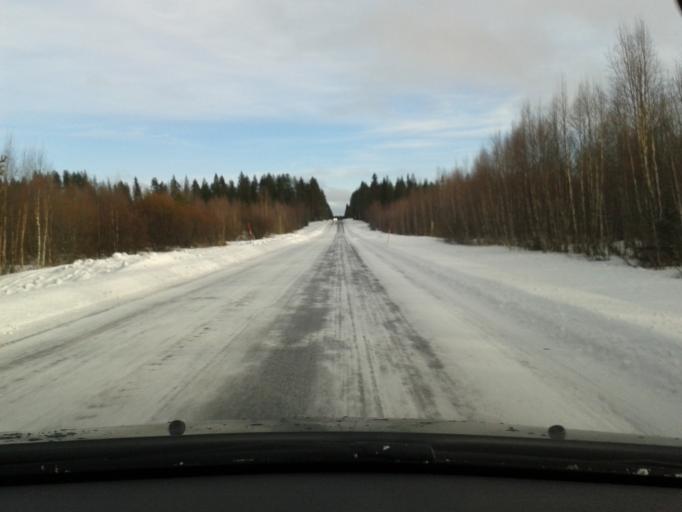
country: SE
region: Vaesterbotten
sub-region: Vilhelmina Kommun
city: Vilhelmina
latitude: 64.6414
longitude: 16.4780
